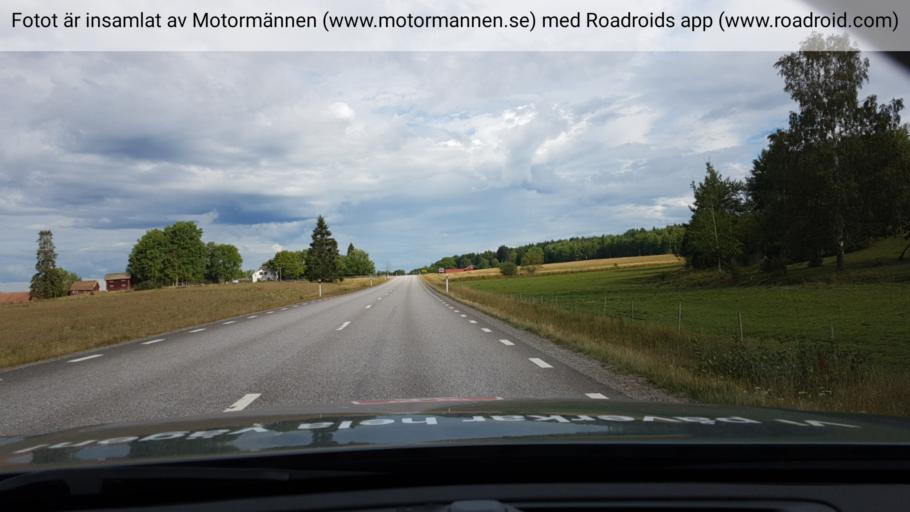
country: SE
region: Uppsala
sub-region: Heby Kommun
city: Morgongava
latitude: 59.8916
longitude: 16.9052
